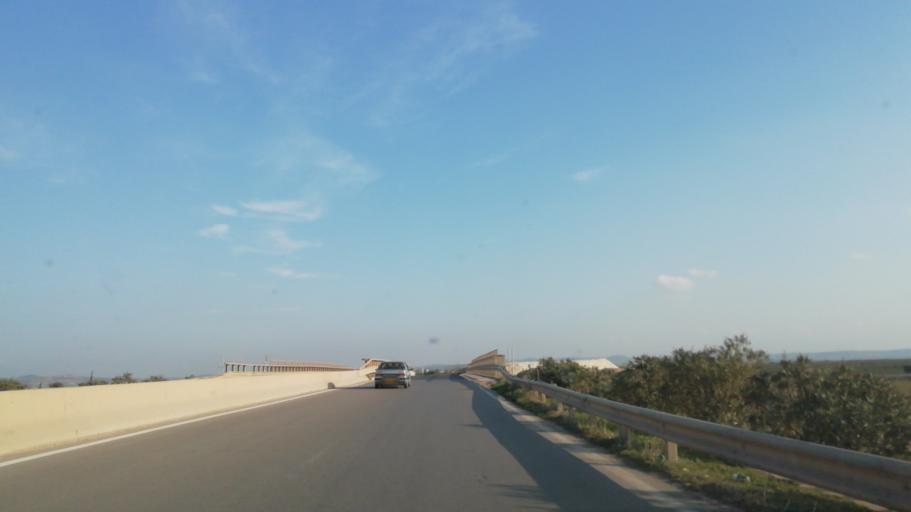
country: DZ
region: Relizane
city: Djidiouia
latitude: 35.8973
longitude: 0.7103
